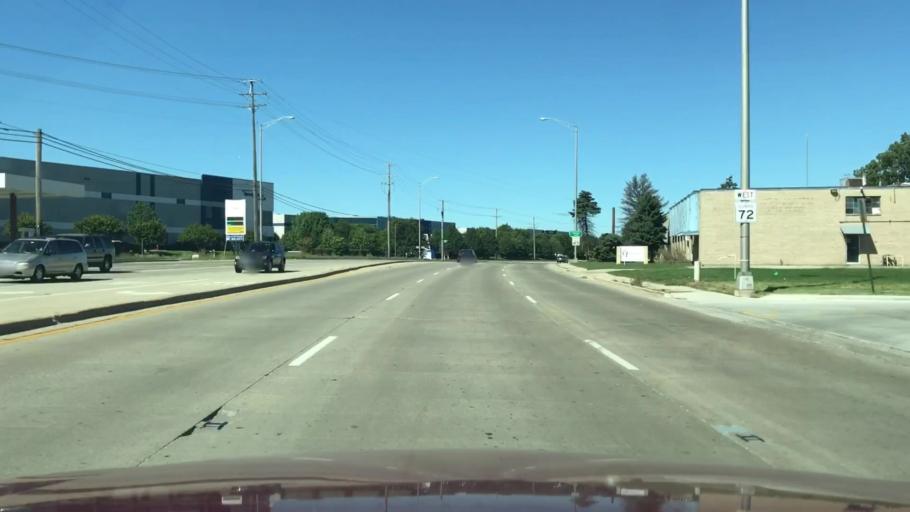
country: US
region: Illinois
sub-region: Cook County
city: Elk Grove Village
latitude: 42.0085
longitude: -87.9409
